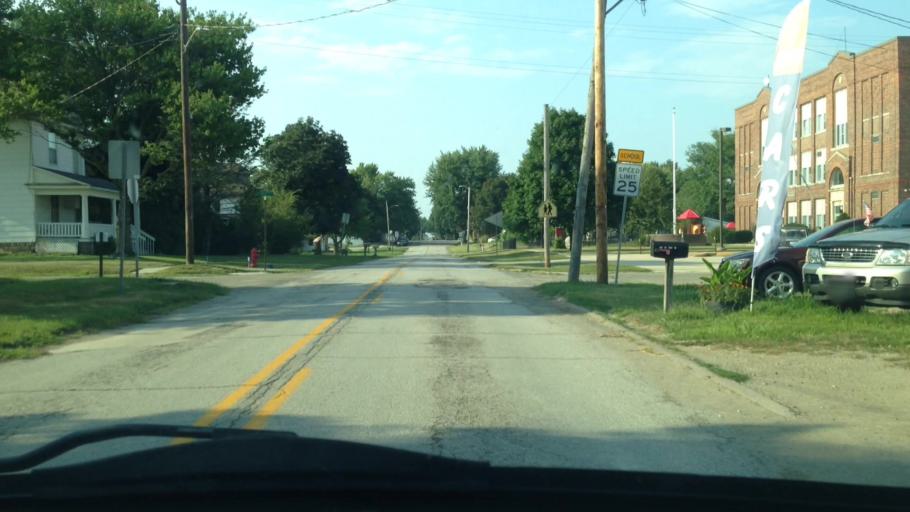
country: US
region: Iowa
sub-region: Henry County
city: Winfield
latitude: 41.2118
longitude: -91.5388
